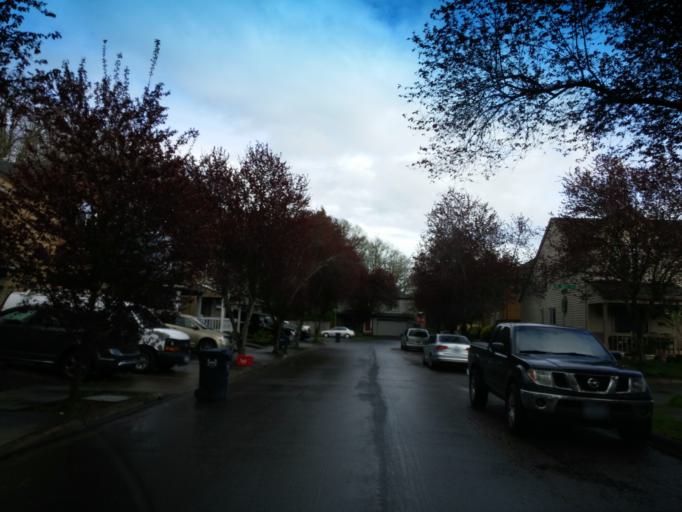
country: US
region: Oregon
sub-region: Washington County
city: Aloha
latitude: 45.5116
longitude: -122.8658
